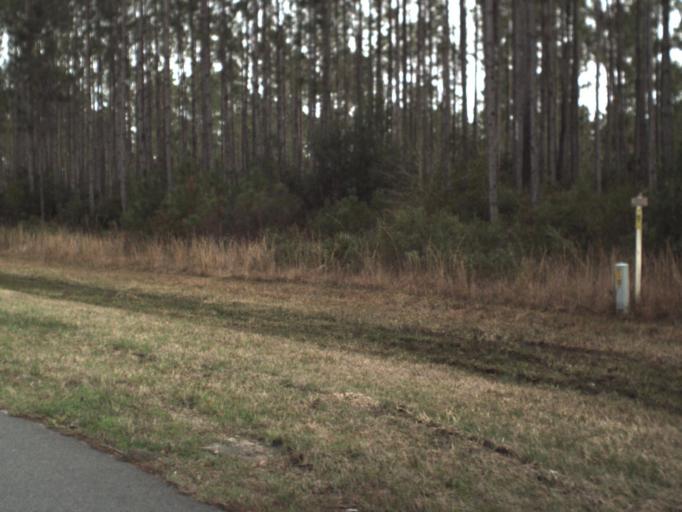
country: US
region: Florida
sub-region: Bay County
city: Callaway
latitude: 30.1427
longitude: -85.4201
